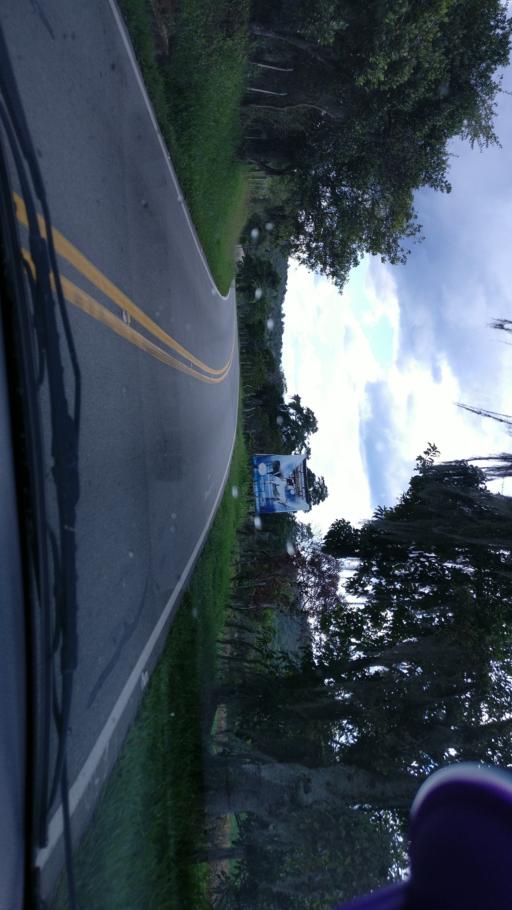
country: CO
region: Santander
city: Curiti
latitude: 6.6363
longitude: -73.0686
